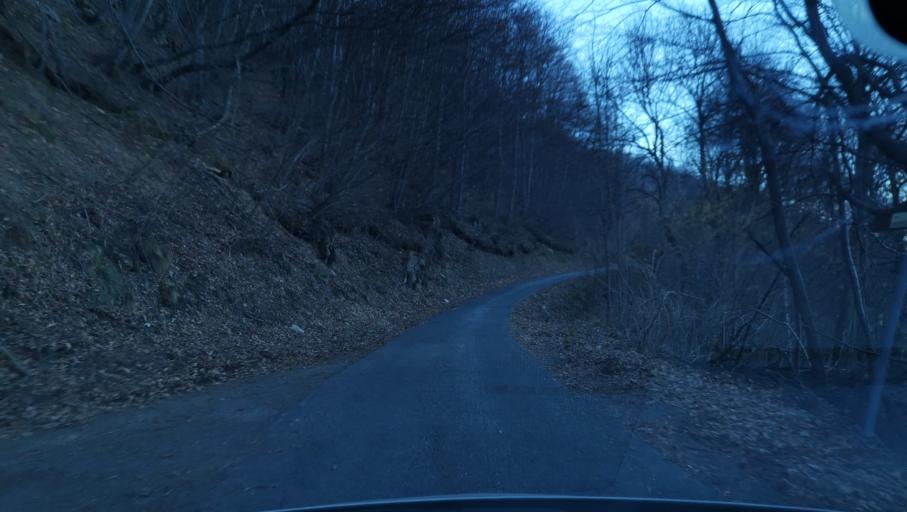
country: IT
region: Piedmont
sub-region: Provincia di Torino
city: Rora
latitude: 44.7749
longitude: 7.1980
